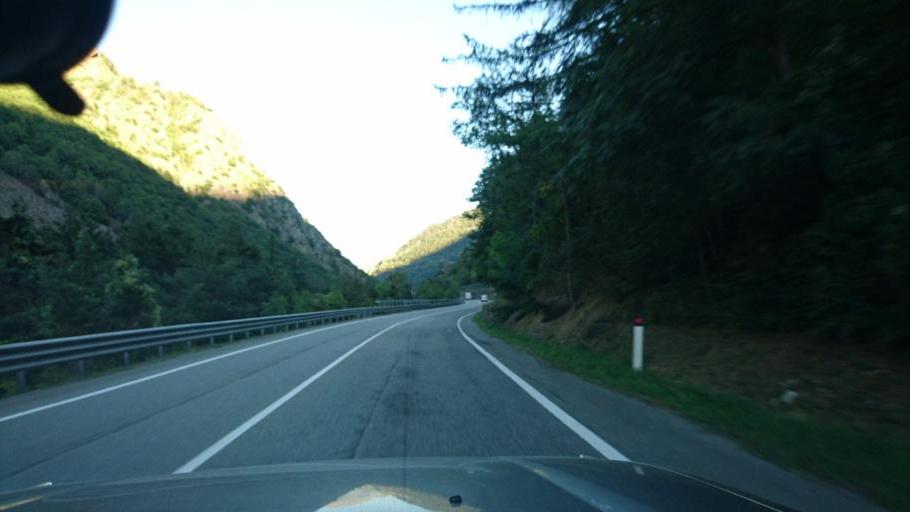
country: IT
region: Aosta Valley
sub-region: Valle d'Aosta
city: Avise
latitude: 45.7125
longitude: 7.1152
